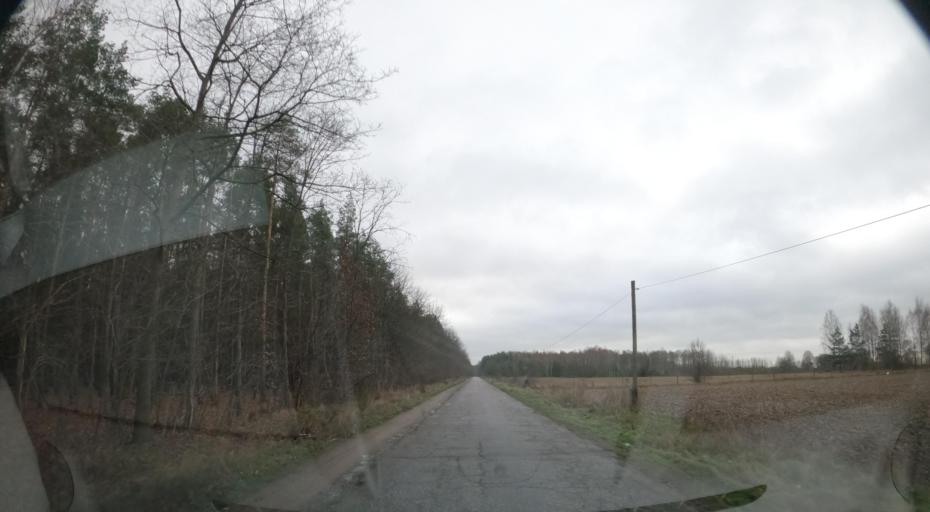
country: PL
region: Greater Poland Voivodeship
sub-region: Powiat zlotowski
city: Krajenka
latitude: 53.2867
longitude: 17.0203
